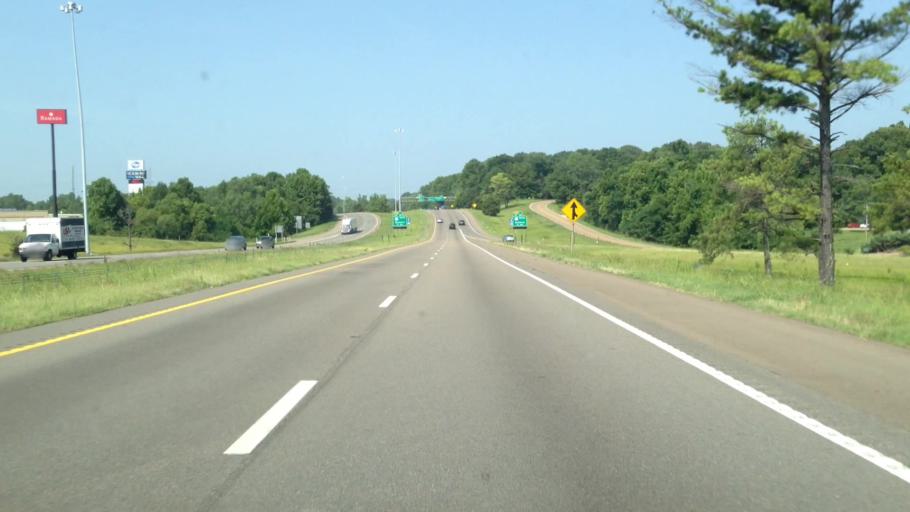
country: US
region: Mississippi
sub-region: Warren County
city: Vicksburg
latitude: 32.3182
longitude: -90.8793
